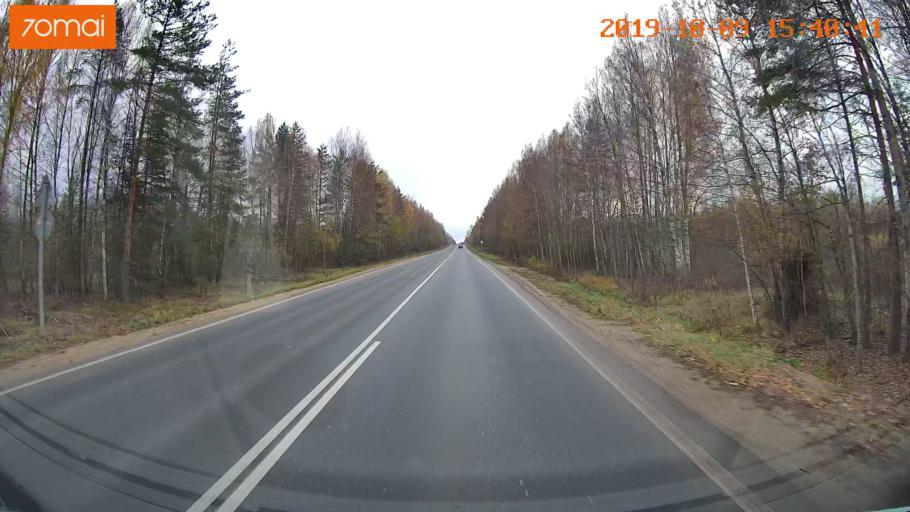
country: RU
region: Kostroma
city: Oktyabr'skiy
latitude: 57.8853
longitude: 41.1395
